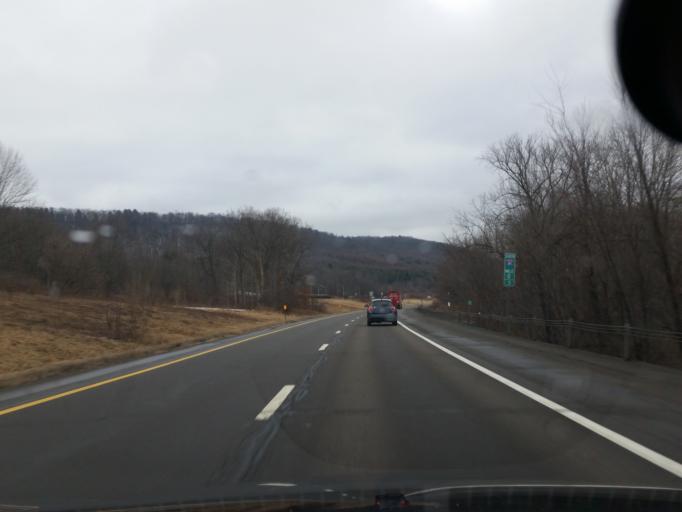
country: US
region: Pennsylvania
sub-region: Susquehanna County
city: Hallstead
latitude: 42.0051
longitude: -75.7557
